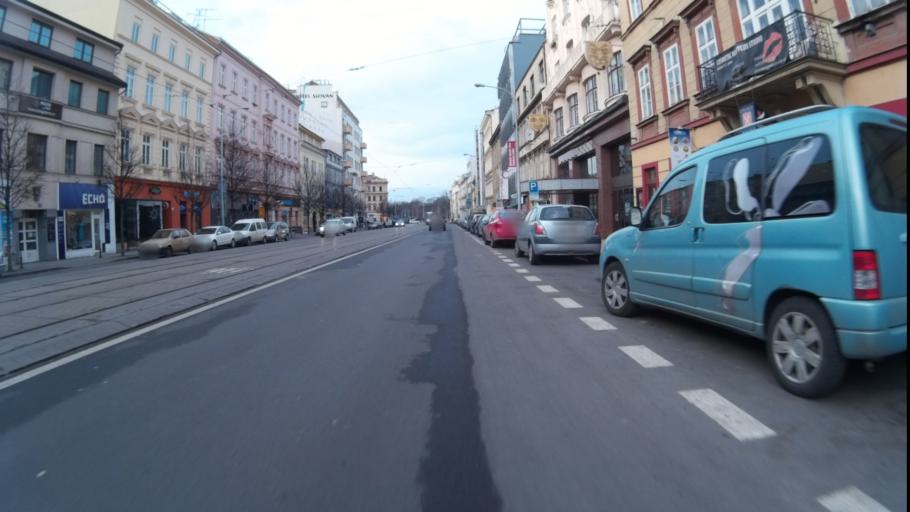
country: CZ
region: South Moravian
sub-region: Mesto Brno
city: Brno
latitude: 49.2017
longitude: 16.6075
